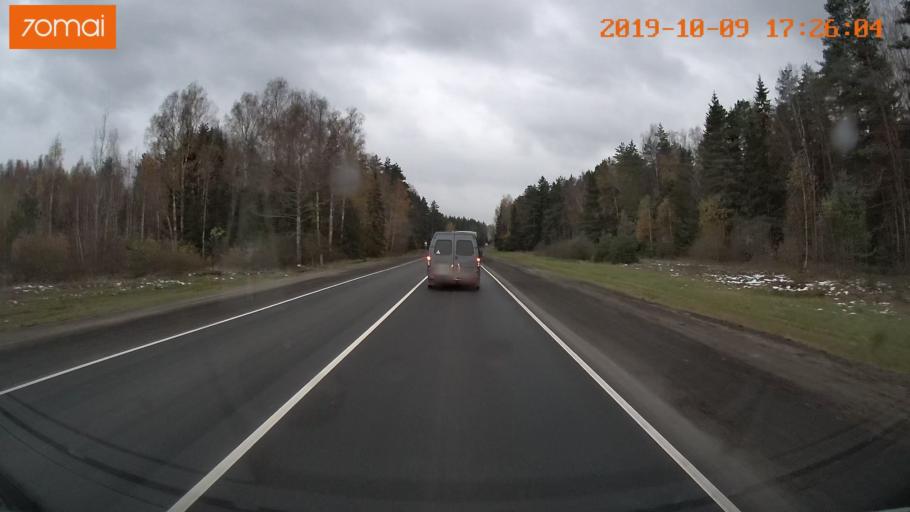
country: RU
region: Ivanovo
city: Furmanov
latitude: 57.1768
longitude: 41.0824
